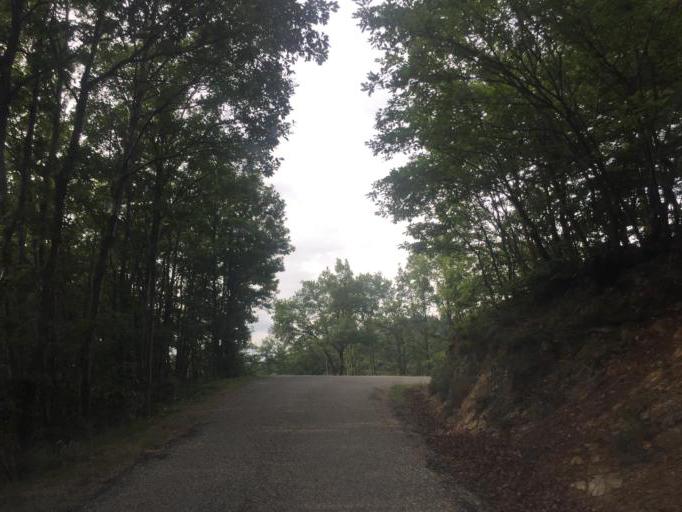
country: FR
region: Rhone-Alpes
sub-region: Departement de l'Ardeche
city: Flaviac
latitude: 44.7924
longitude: 4.6550
